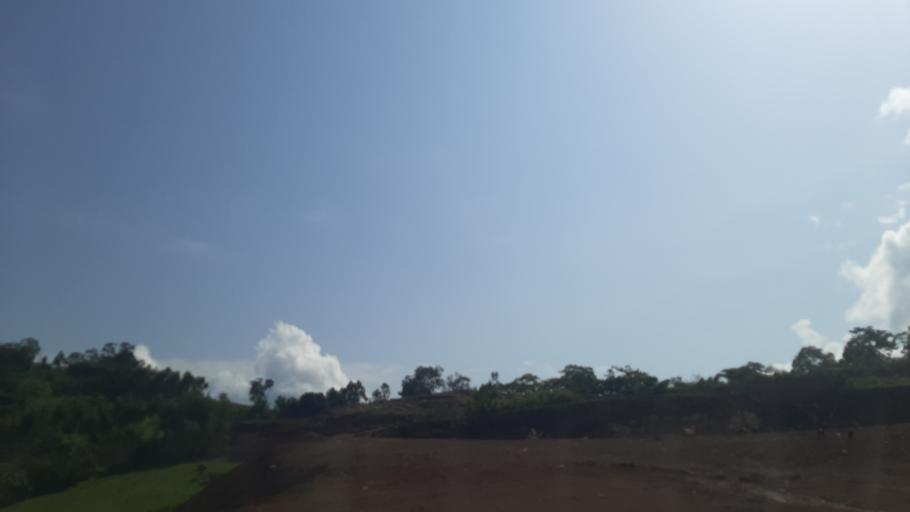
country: ET
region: Oromiya
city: Agaro
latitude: 7.9127
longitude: 36.8056
